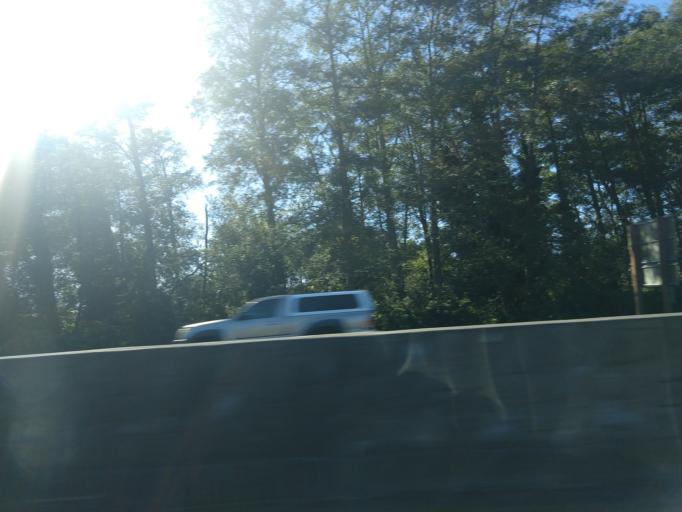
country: US
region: California
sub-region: Humboldt County
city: Fortuna
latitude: 40.5837
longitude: -124.1519
